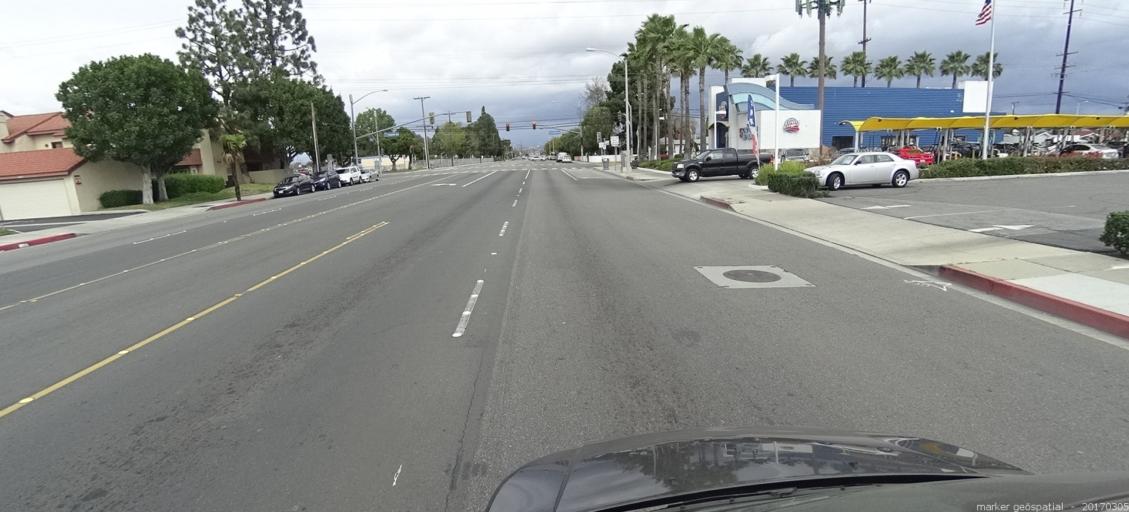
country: US
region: California
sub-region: Orange County
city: Buena Park
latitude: 33.8388
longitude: -117.9760
